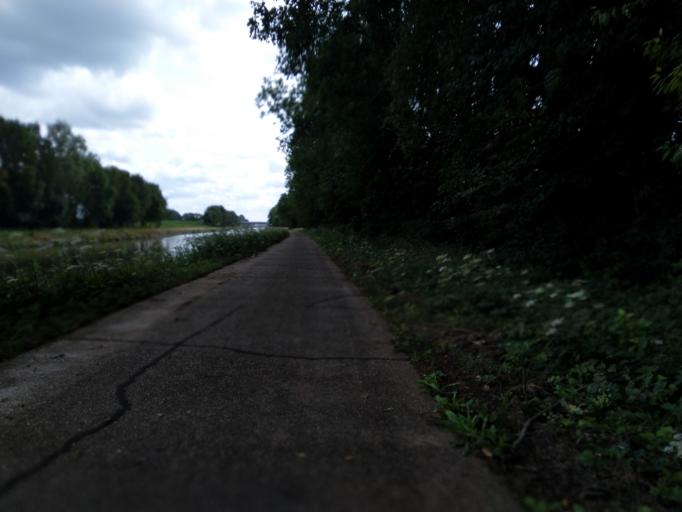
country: BE
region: Wallonia
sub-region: Province du Hainaut
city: Hensies
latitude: 50.4758
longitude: 3.7301
